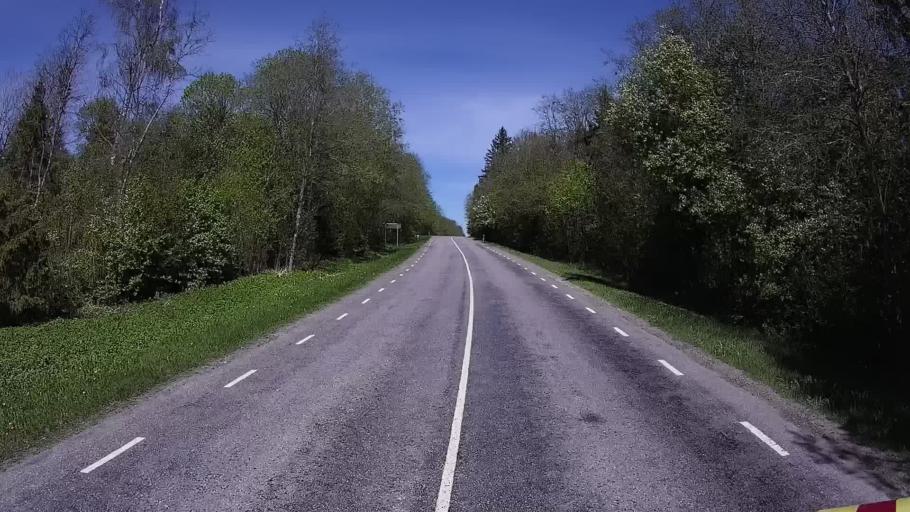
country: EE
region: Raplamaa
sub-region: Kehtna vald
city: Kehtna
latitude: 59.0574
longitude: 25.1388
